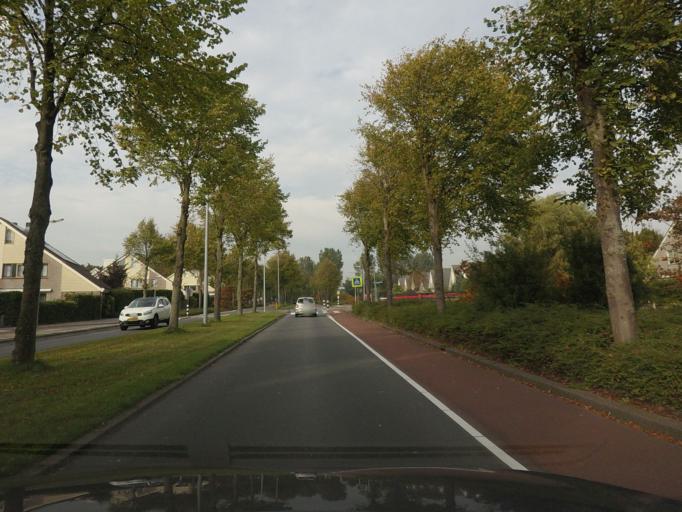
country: NL
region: North Holland
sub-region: Gemeente Langedijk
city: Broek op Langedijk
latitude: 52.6669
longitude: 4.7716
